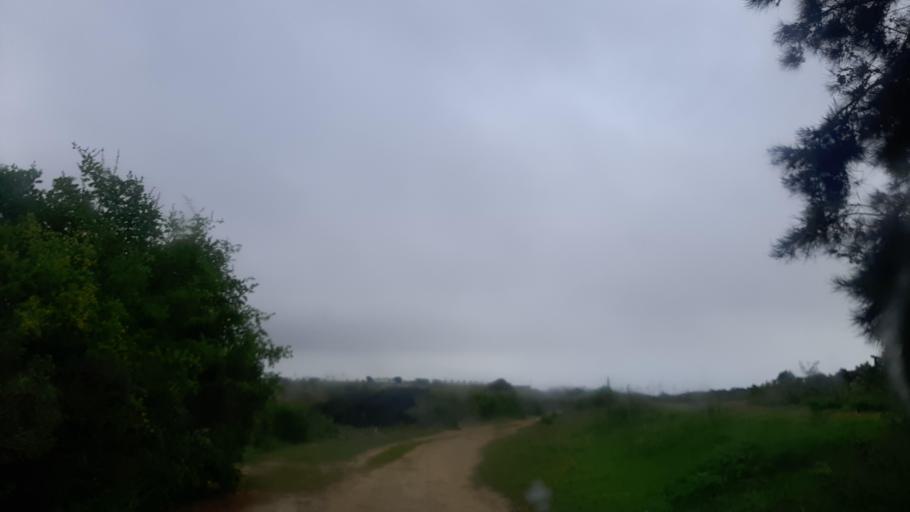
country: TN
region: Nabul
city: Qulaybiyah
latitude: 36.8247
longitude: 11.0412
